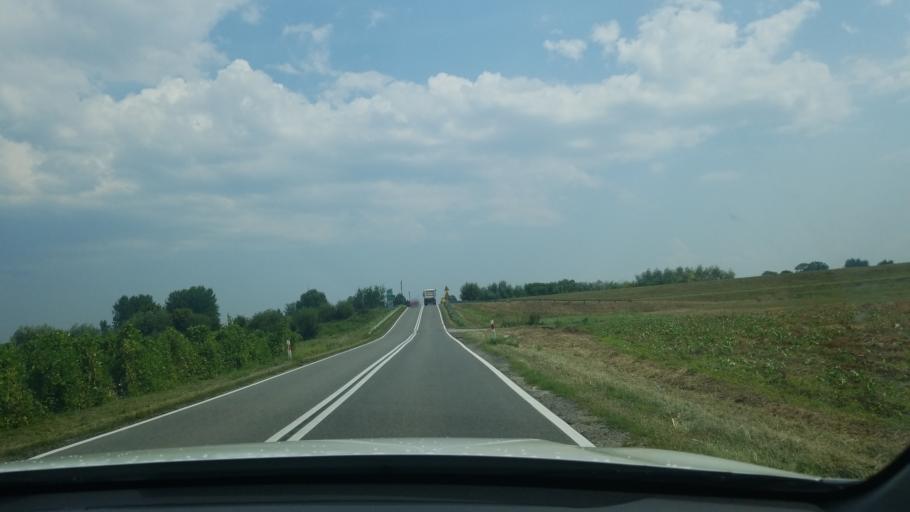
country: PL
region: Lesser Poland Voivodeship
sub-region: Powiat bochenski
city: Dziewin
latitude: 50.1180
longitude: 20.5065
